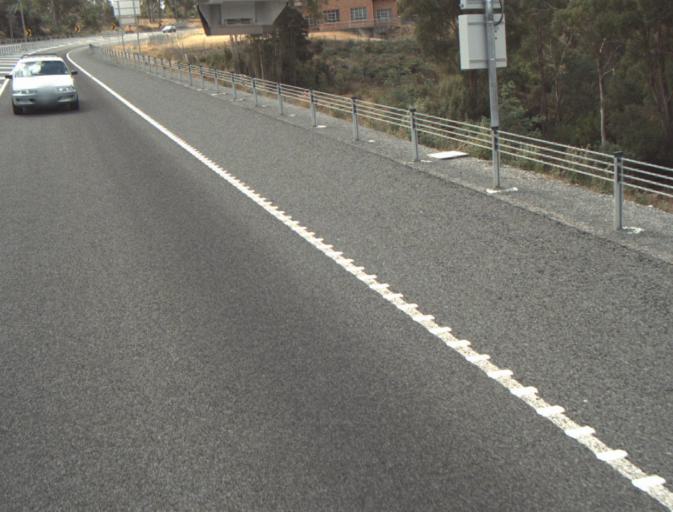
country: AU
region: Tasmania
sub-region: Launceston
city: Mayfield
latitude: -41.3006
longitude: 147.0499
